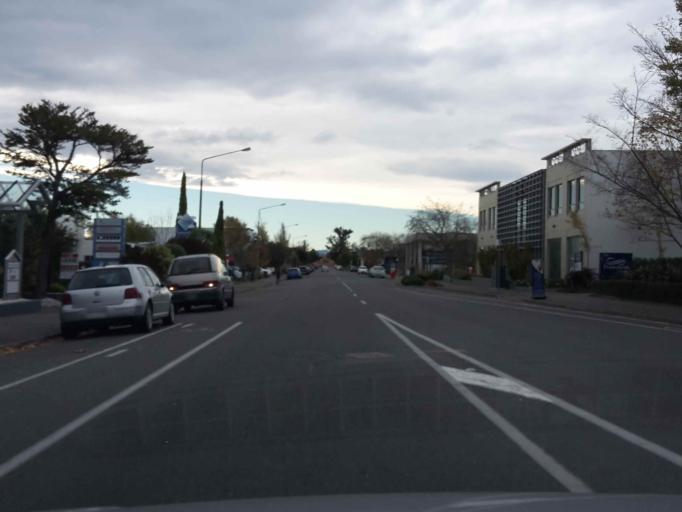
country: NZ
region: Canterbury
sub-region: Christchurch City
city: Christchurch
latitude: -43.5347
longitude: 172.6068
